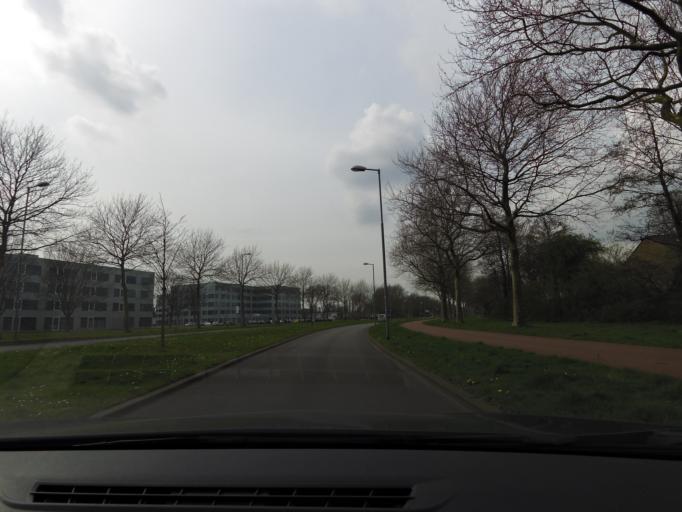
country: NL
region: South Holland
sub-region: Gemeente Spijkenisse
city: Spijkenisse
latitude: 51.8569
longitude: 4.3629
